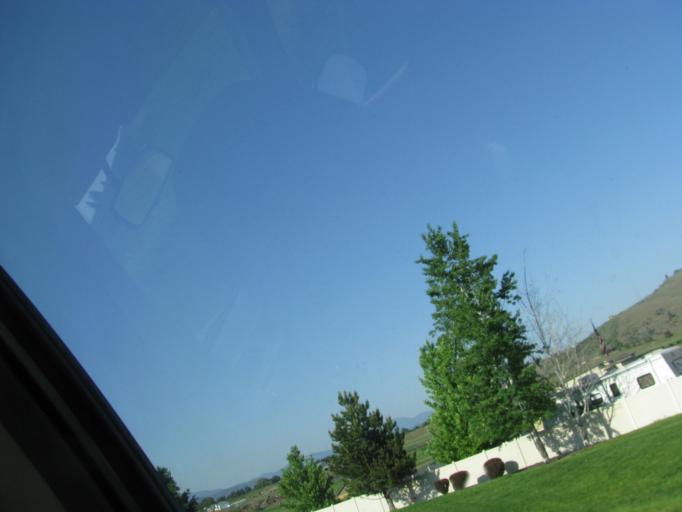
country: US
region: Washington
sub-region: Spokane County
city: Liberty Lake
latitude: 47.6381
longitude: -117.1484
